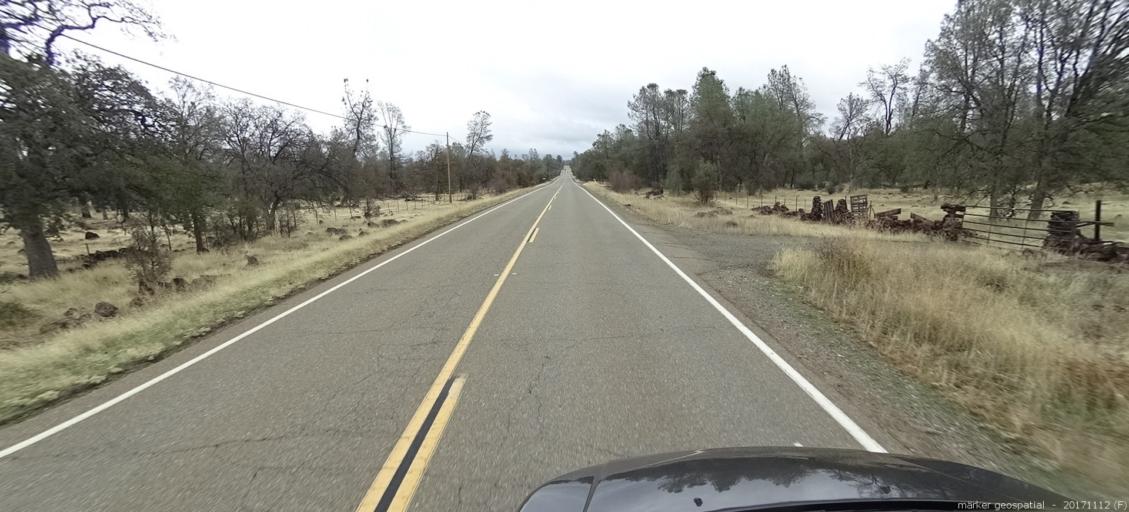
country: US
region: California
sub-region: Shasta County
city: Palo Cedro
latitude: 40.4812
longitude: -122.1029
